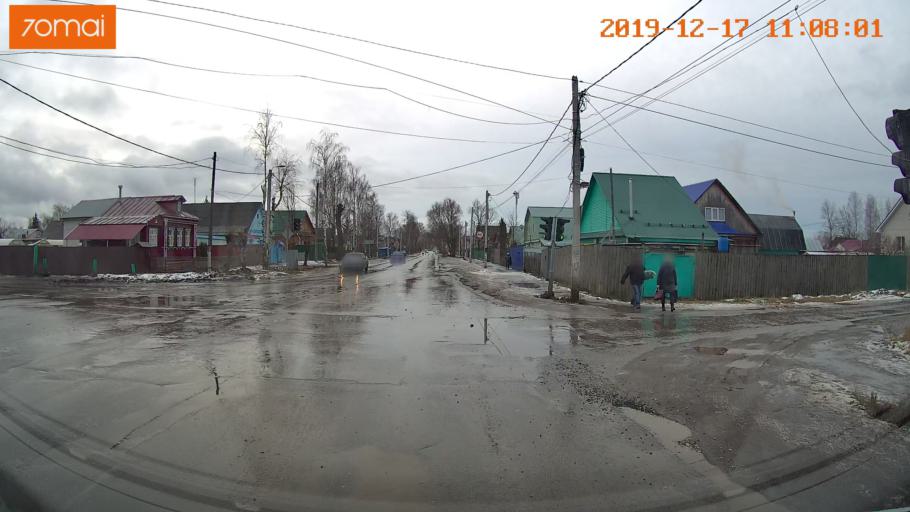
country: RU
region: Vladimir
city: Gus'-Khrustal'nyy
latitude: 55.6079
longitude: 40.6433
